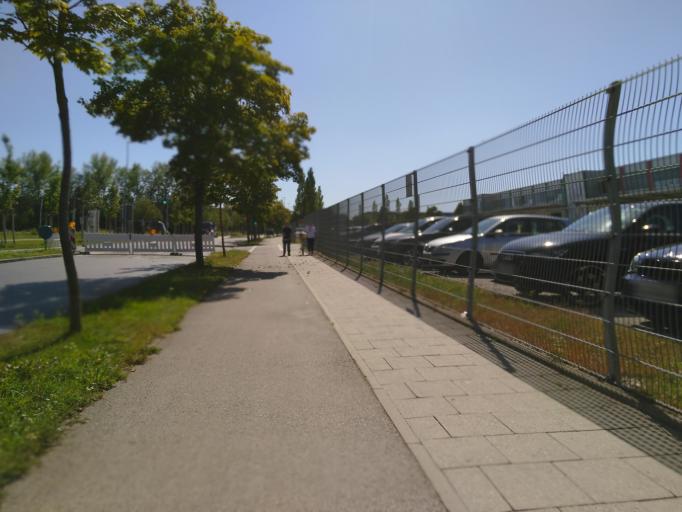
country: DE
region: Bavaria
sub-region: Upper Bavaria
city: Unterfoehring
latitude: 48.1998
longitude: 11.6052
